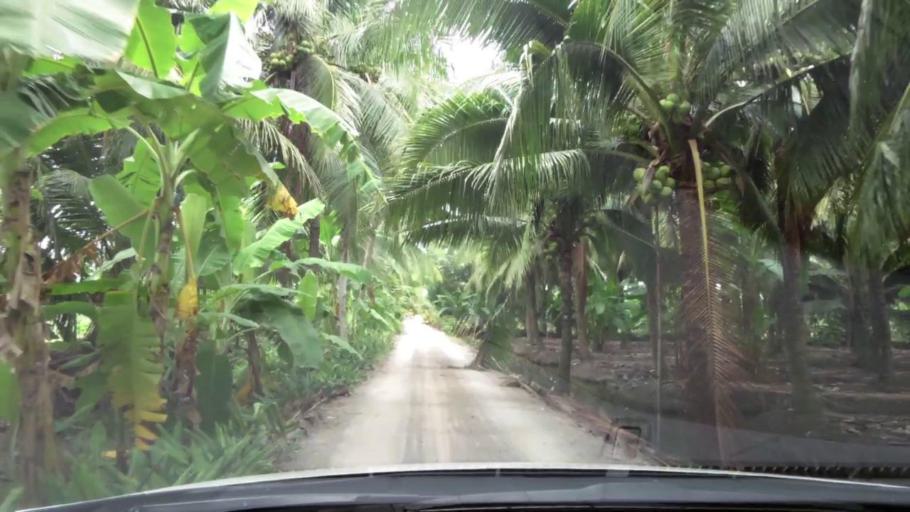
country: TH
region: Ratchaburi
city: Damnoen Saduak
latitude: 13.5551
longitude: 99.9866
